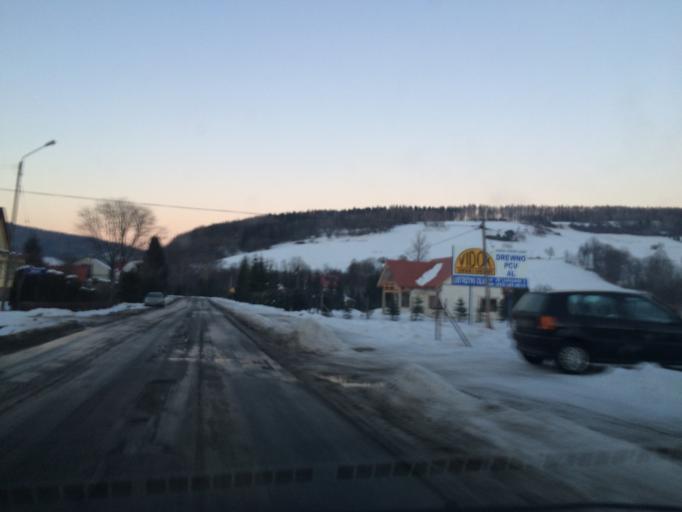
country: PL
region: Subcarpathian Voivodeship
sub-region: Powiat bieszczadzki
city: Ustrzyki Dolne
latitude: 49.4194
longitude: 22.5747
